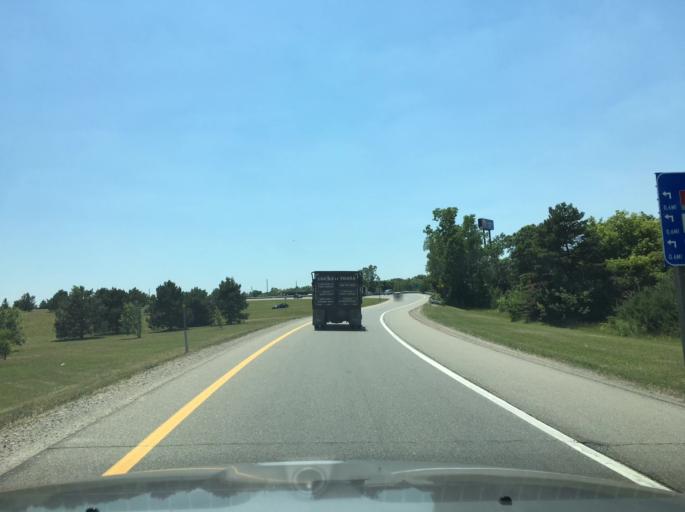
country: US
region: Michigan
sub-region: Macomb County
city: Utica
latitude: 42.6289
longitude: -83.0137
